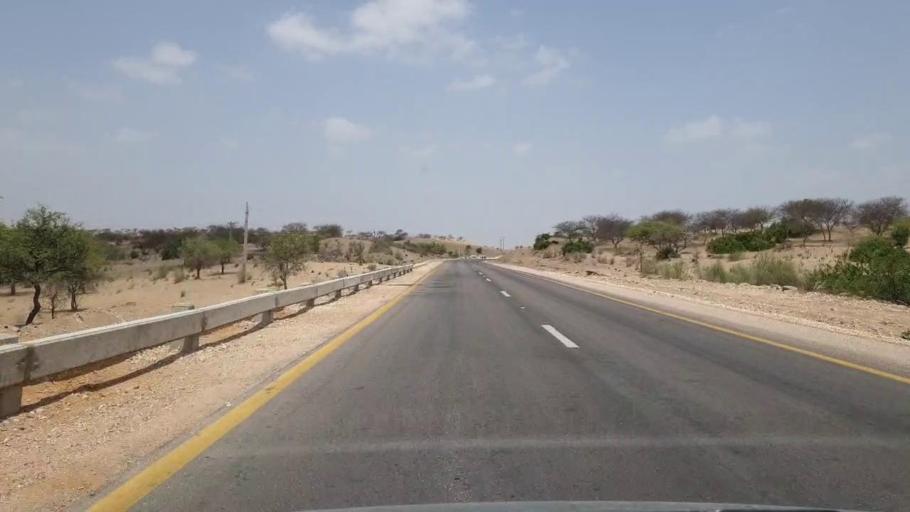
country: PK
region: Sindh
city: Mithi
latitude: 24.7986
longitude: 69.7414
